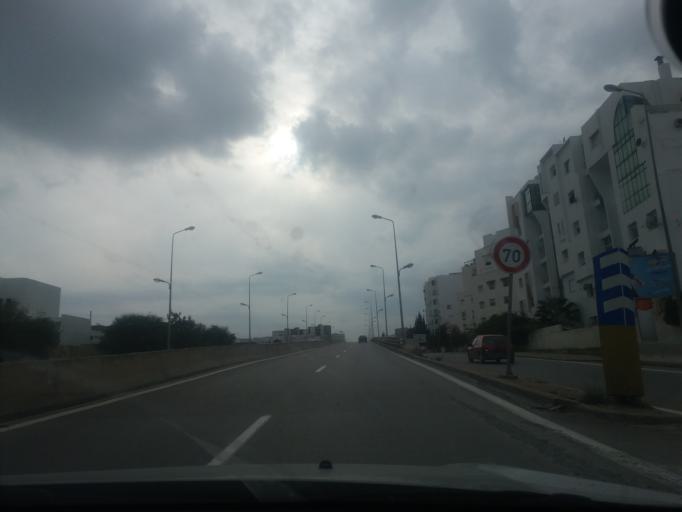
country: TN
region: Ariana
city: Ariana
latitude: 36.8589
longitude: 10.1690
